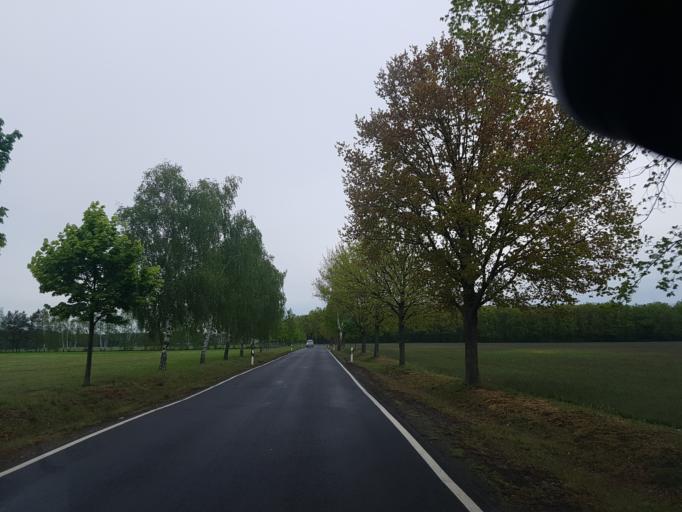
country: DE
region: Brandenburg
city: Spremberg
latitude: 51.6374
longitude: 14.4333
